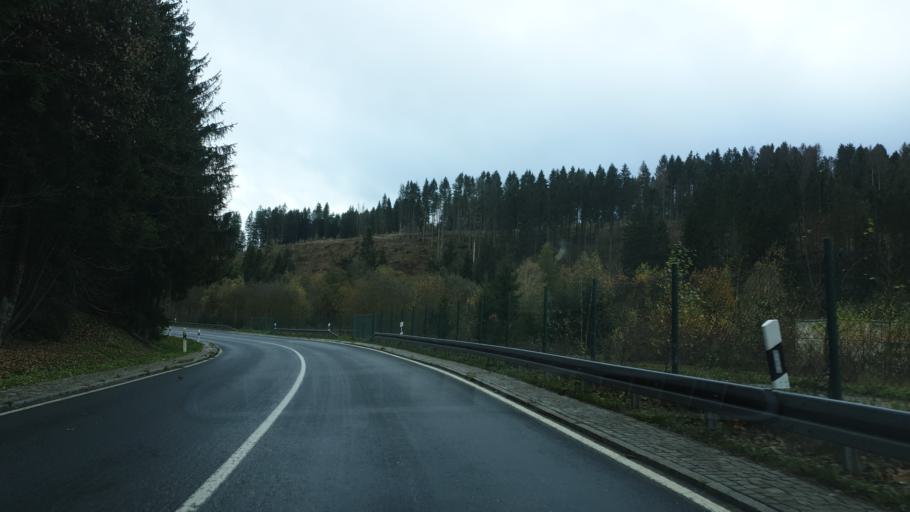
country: DE
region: Saxony
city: Schoenheide
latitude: 50.4937
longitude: 12.5452
